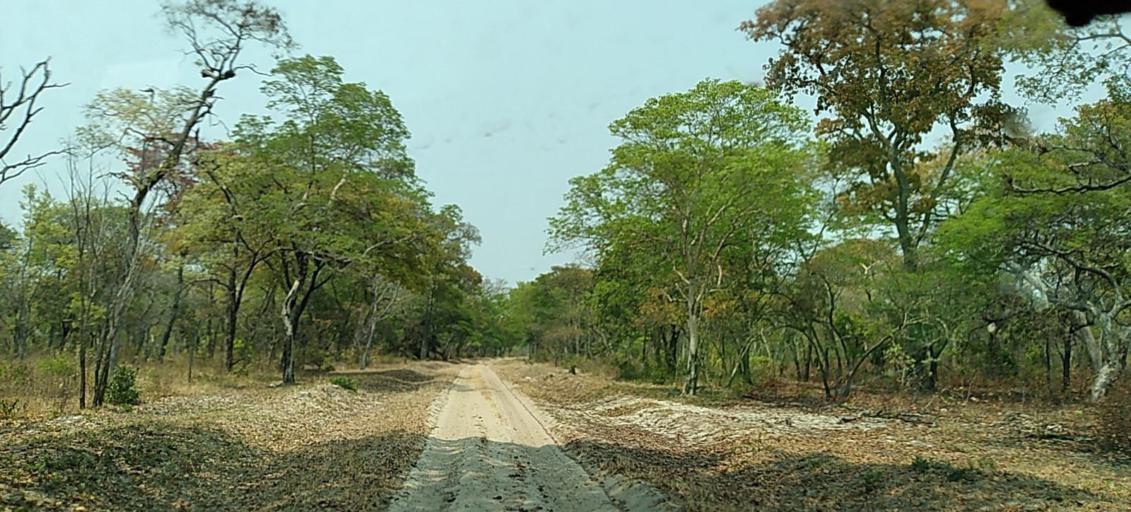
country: ZM
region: North-Western
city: Zambezi
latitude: -13.9305
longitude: 23.2246
